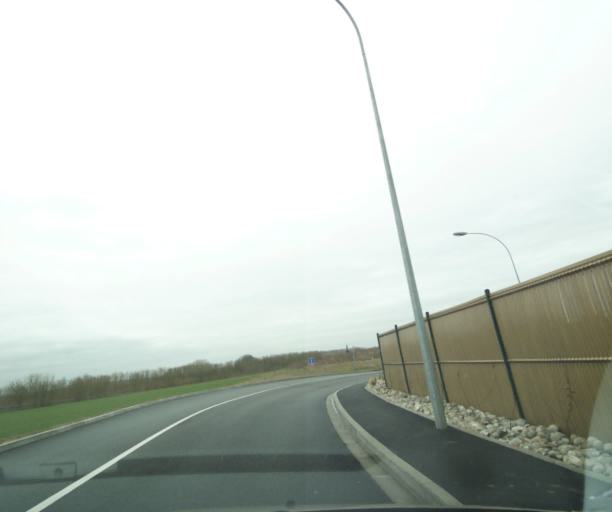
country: FR
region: Picardie
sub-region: Departement de l'Oise
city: Noyon
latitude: 49.5748
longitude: 3.0328
